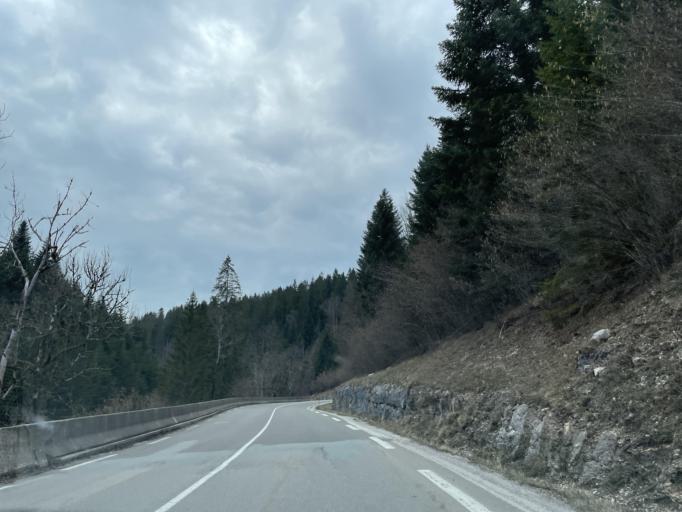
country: FR
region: Franche-Comte
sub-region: Departement du Doubs
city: Gilley
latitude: 47.0156
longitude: 6.4888
